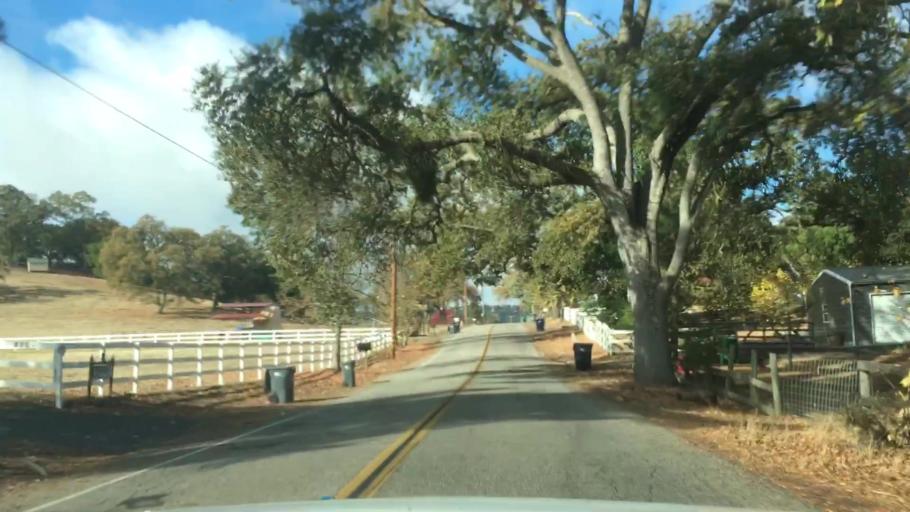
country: US
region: California
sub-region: San Luis Obispo County
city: Atascadero
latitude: 35.4584
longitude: -120.6635
